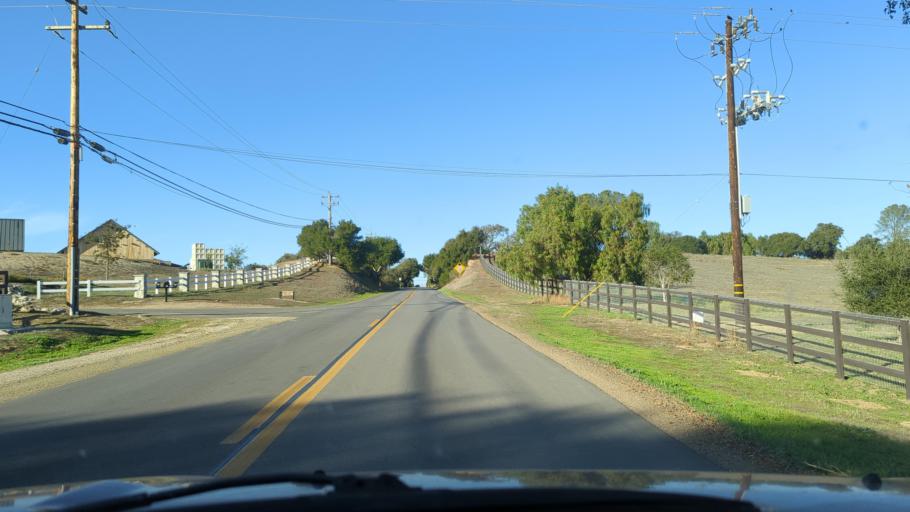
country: US
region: California
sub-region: Santa Barbara County
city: Santa Ynez
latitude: 34.5989
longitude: -120.0983
